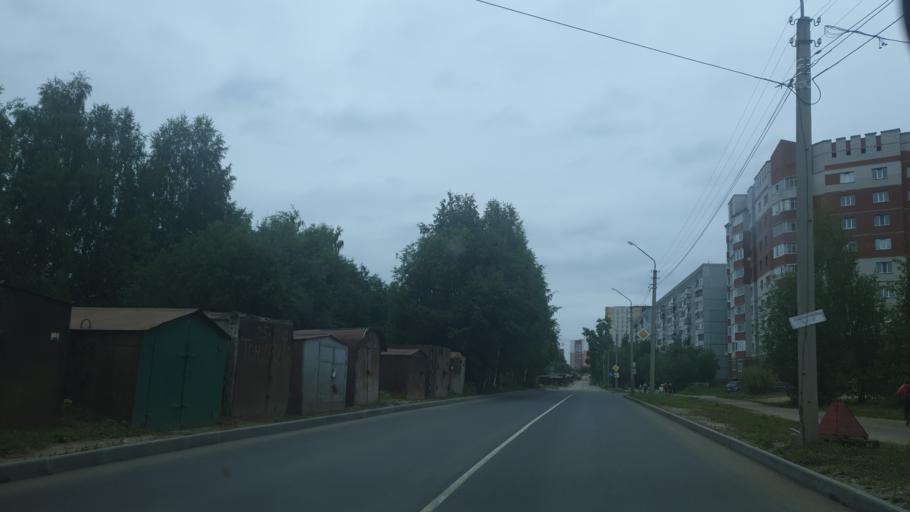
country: RU
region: Komi Republic
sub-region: Syktyvdinskiy Rayon
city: Syktyvkar
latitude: 61.6953
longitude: 50.8069
